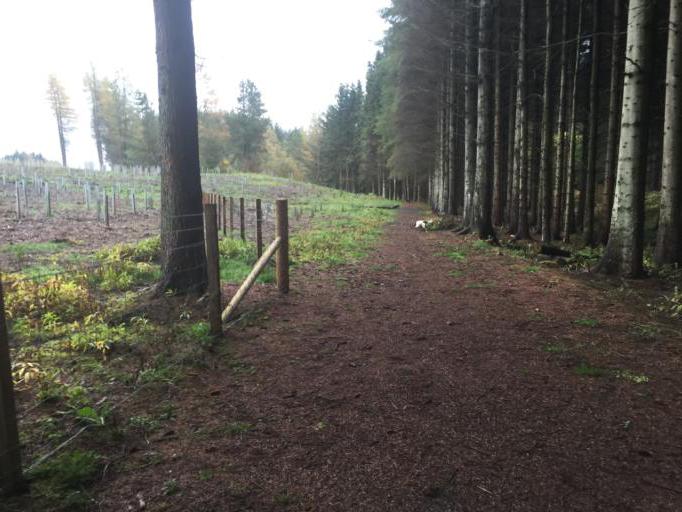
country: GB
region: Scotland
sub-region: West Lothian
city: Linlithgow
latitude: 55.9532
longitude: -3.6005
